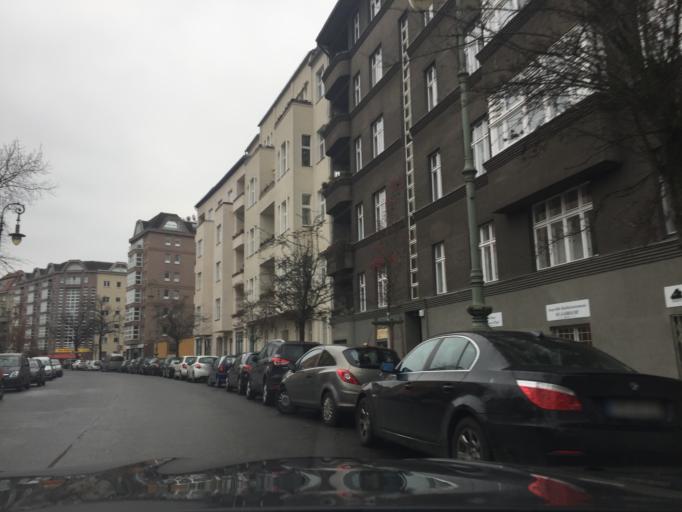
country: DE
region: Berlin
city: Charlottenburg Bezirk
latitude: 52.5078
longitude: 13.2930
